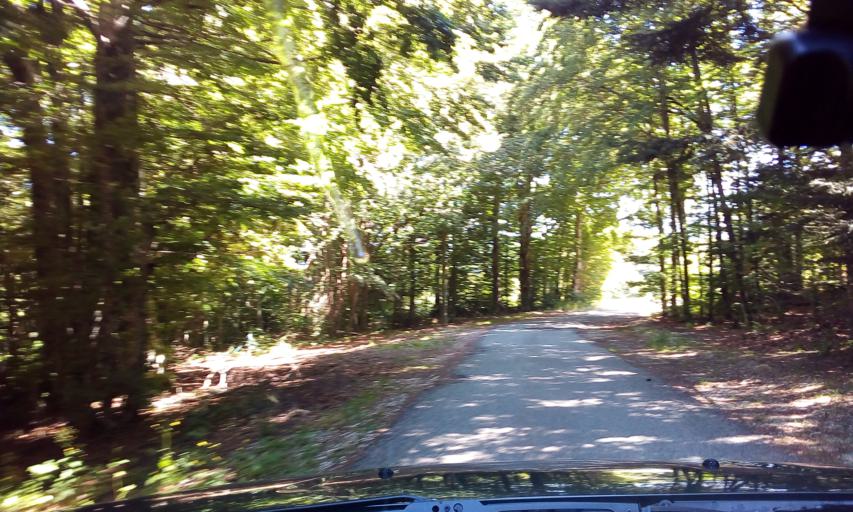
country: FR
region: Rhone-Alpes
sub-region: Departement de la Drome
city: Die
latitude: 44.8656
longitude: 5.3569
